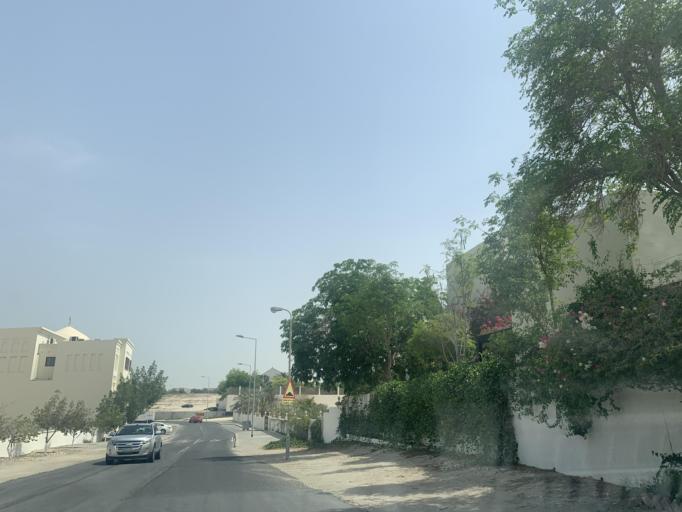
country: BH
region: Northern
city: Madinat `Isa
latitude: 26.1514
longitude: 50.5396
